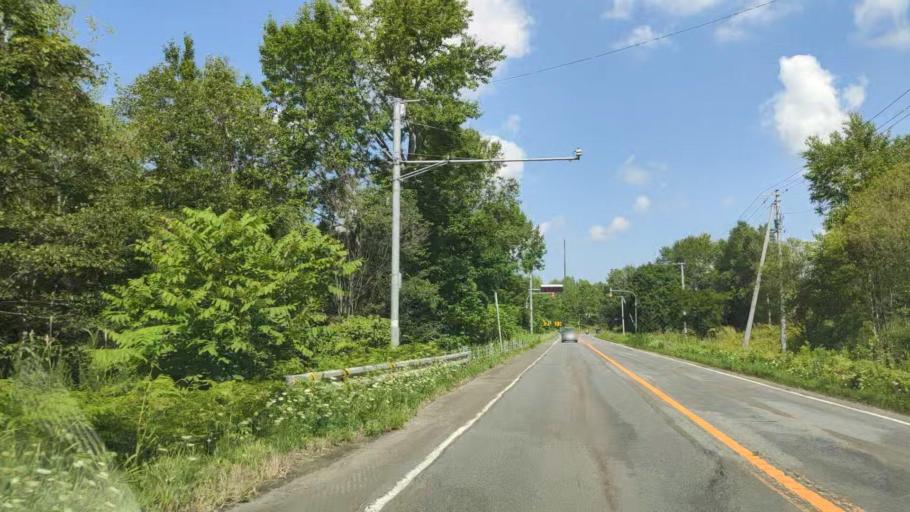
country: JP
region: Hokkaido
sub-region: Asahikawa-shi
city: Asahikawa
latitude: 43.5807
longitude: 142.4377
